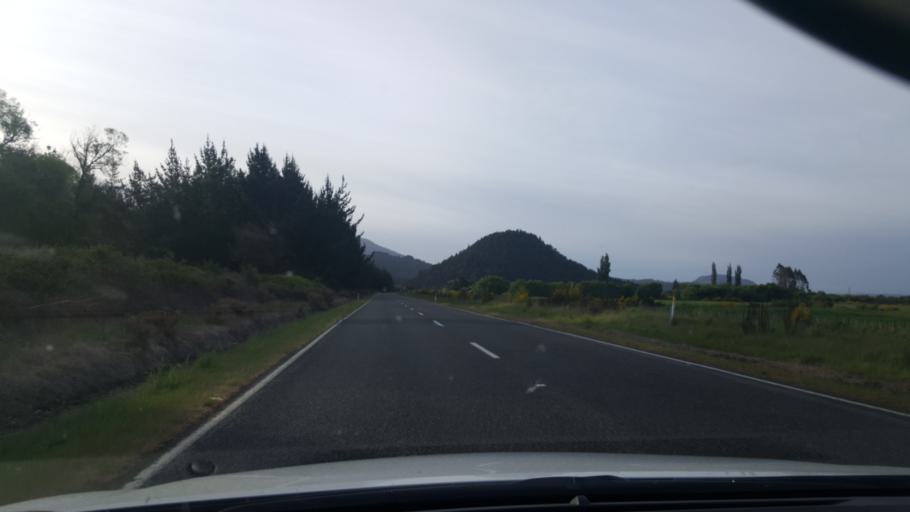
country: NZ
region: Waikato
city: Turangi
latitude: -38.9859
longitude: 175.7859
